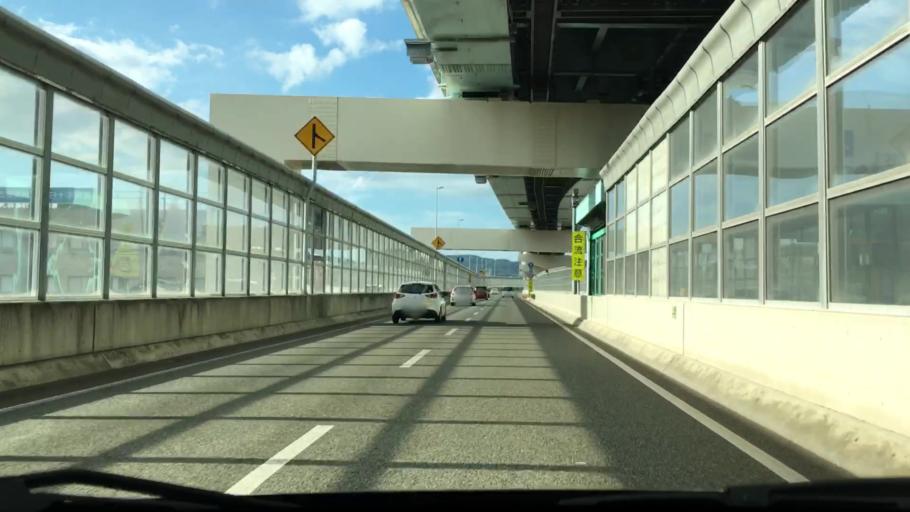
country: JP
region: Fukuoka
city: Fukuoka-shi
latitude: 33.5736
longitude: 130.3163
